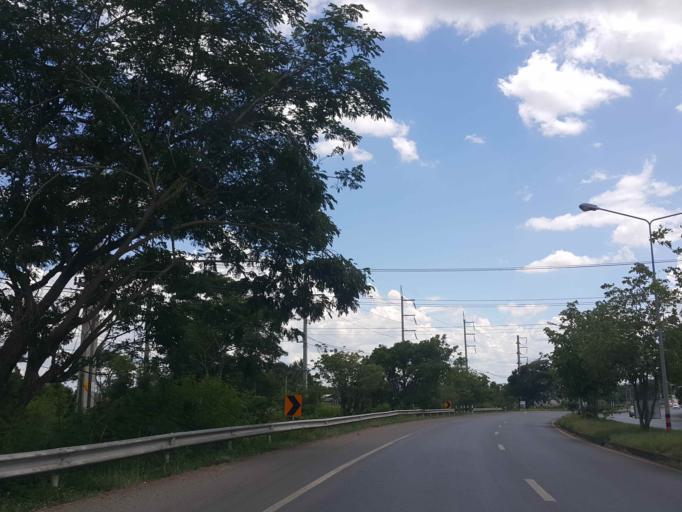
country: TH
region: Phrae
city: Nong Muang Khai
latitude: 18.2286
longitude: 100.2103
